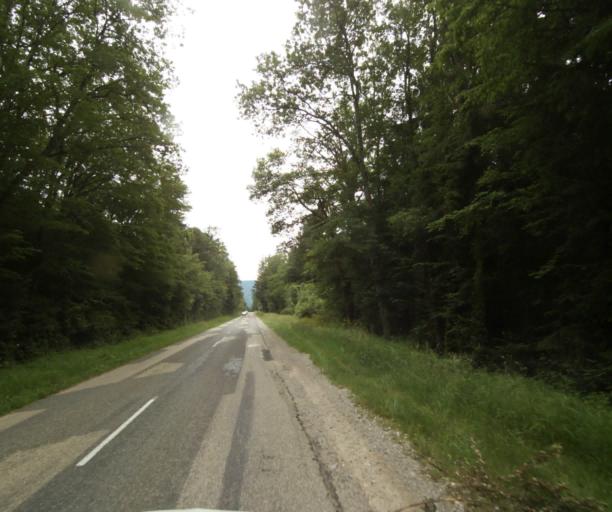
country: FR
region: Rhone-Alpes
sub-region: Departement de la Haute-Savoie
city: Sciez
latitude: 46.3113
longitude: 6.4047
